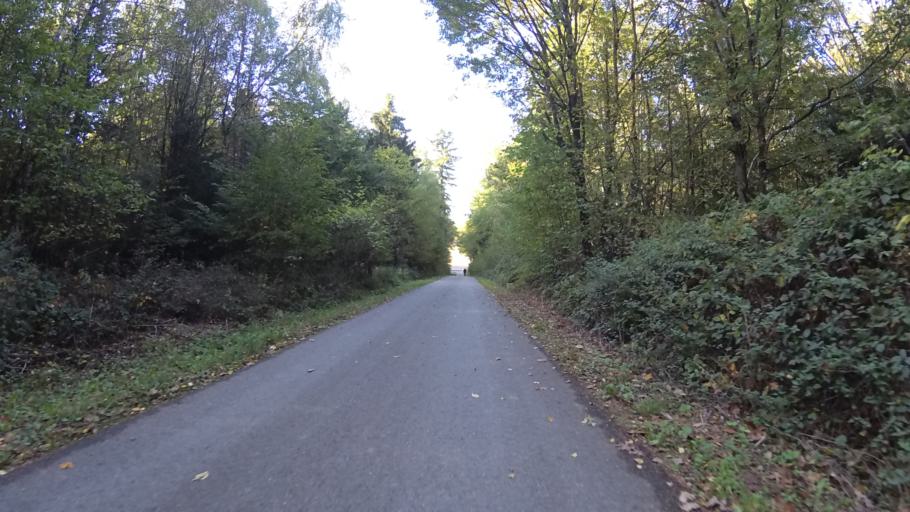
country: DE
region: Saarland
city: Sankt Wendel
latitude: 49.4530
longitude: 7.1959
